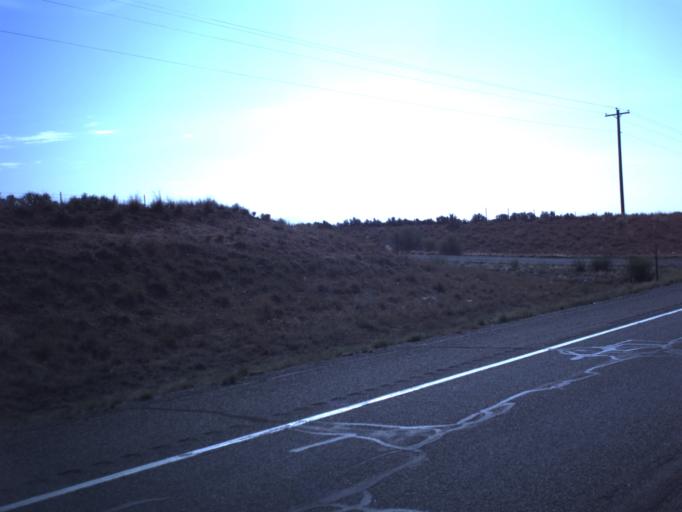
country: US
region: Utah
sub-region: San Juan County
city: Blanding
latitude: 37.5013
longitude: -109.4861
